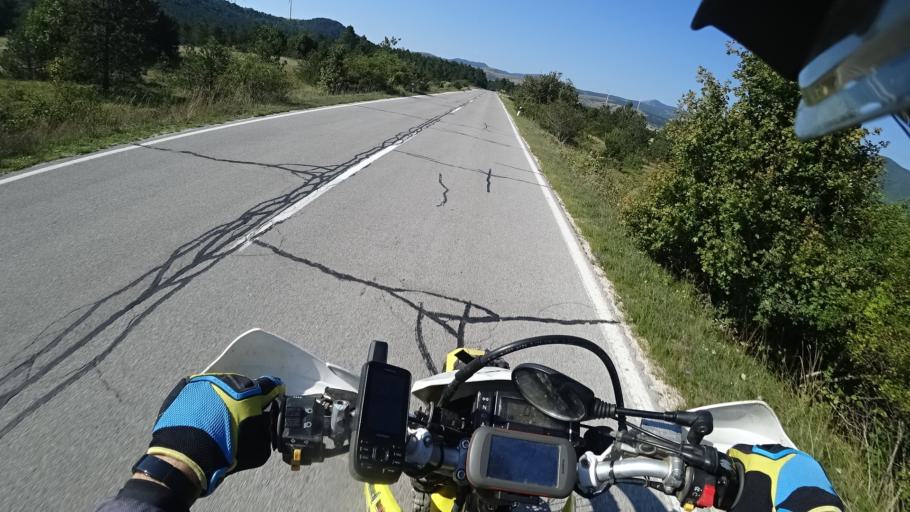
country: HR
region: Zadarska
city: Gracac
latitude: 44.2887
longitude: 16.0789
